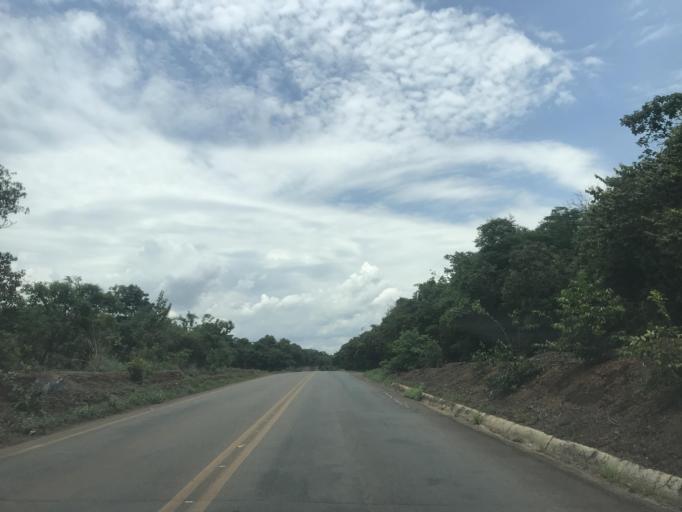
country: BR
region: Goias
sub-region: Vianopolis
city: Vianopolis
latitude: -16.7231
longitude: -48.4101
